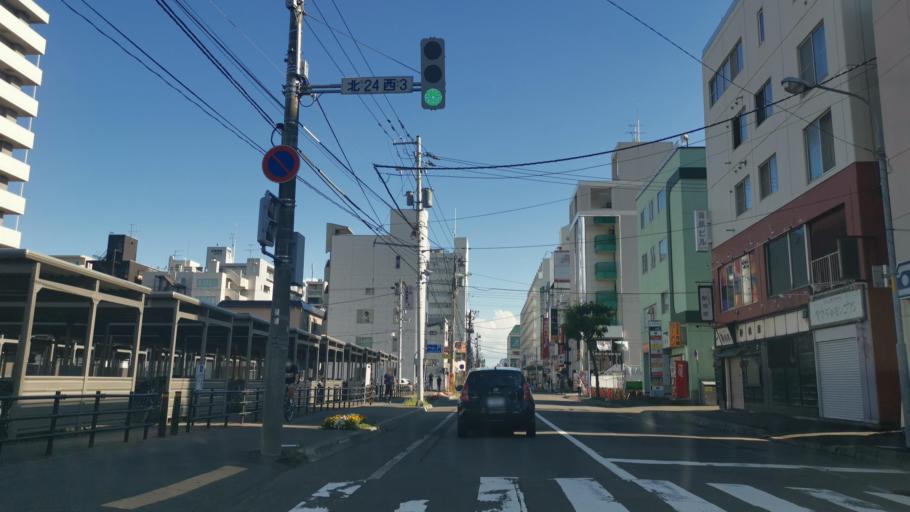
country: JP
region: Hokkaido
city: Sapporo
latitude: 43.0917
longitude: 141.3443
